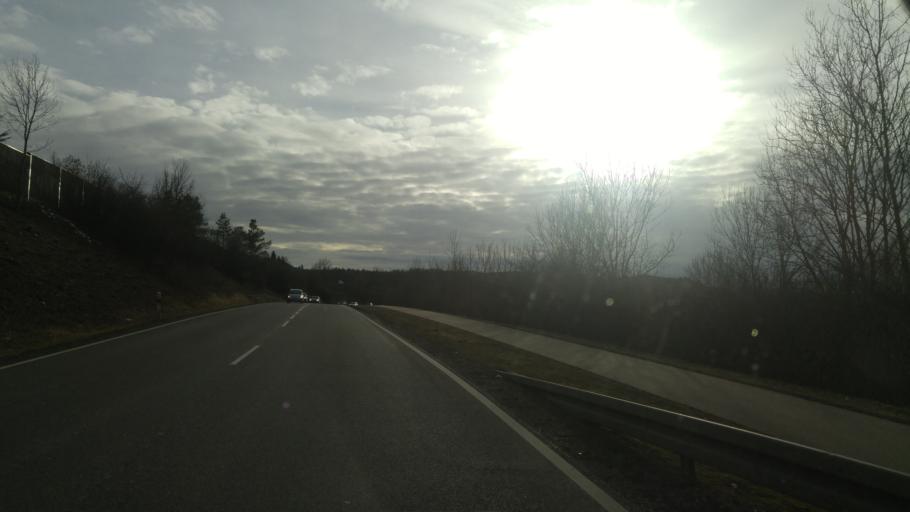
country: DE
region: Baden-Wuerttemberg
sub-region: Regierungsbezirk Stuttgart
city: Leonberg
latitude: 48.7934
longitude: 8.9915
